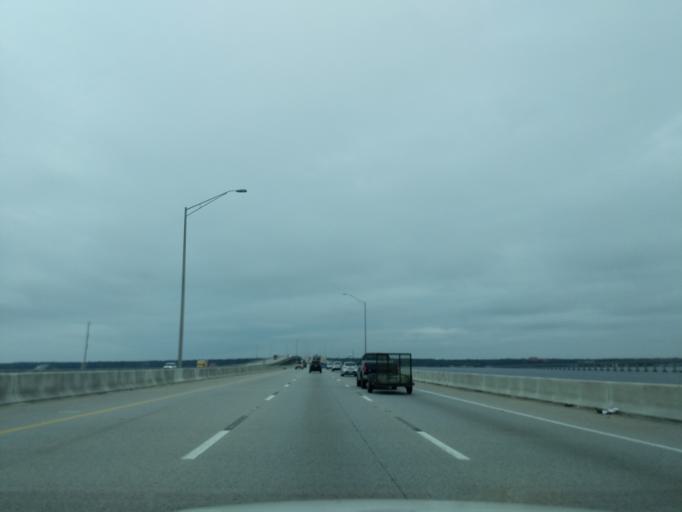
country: US
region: Florida
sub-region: Escambia County
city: Ferry Pass
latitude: 30.5226
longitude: -87.1405
